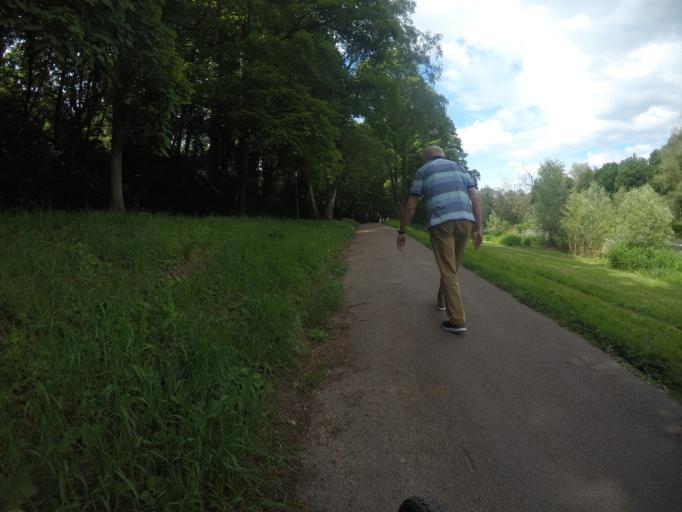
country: DE
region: Baden-Wuerttemberg
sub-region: Karlsruhe Region
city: Pforzheim
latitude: 48.8789
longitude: 8.6977
